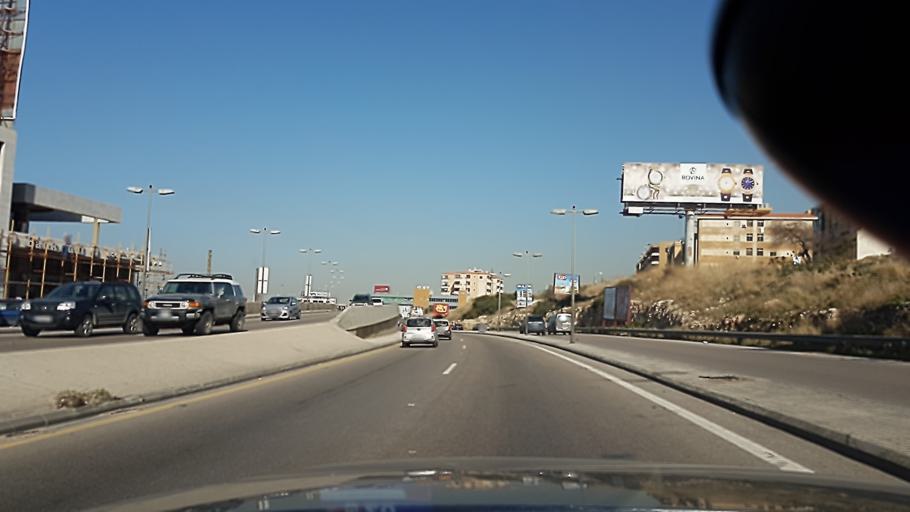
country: LB
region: Mont-Liban
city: Baabda
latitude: 33.7924
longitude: 35.4824
